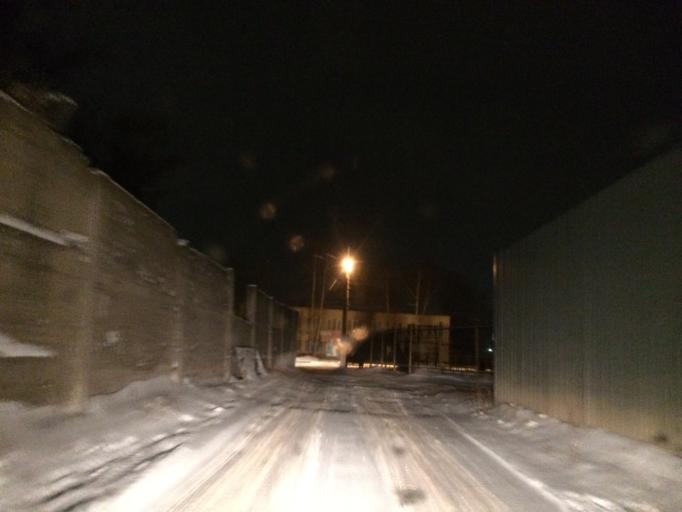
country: RU
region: Tula
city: Tula
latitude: 54.2191
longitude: 37.6820
